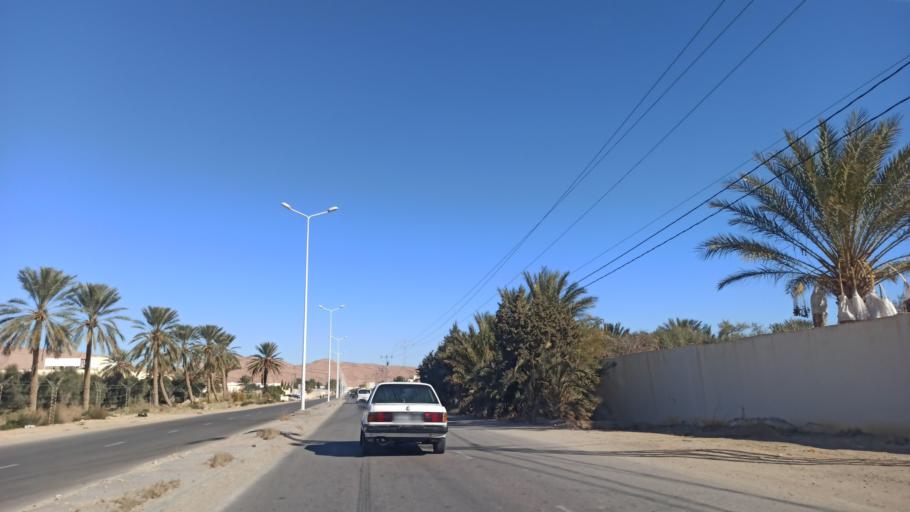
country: TN
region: Gafsa
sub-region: Gafsa Municipality
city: Gafsa
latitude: 34.4081
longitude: 8.7350
